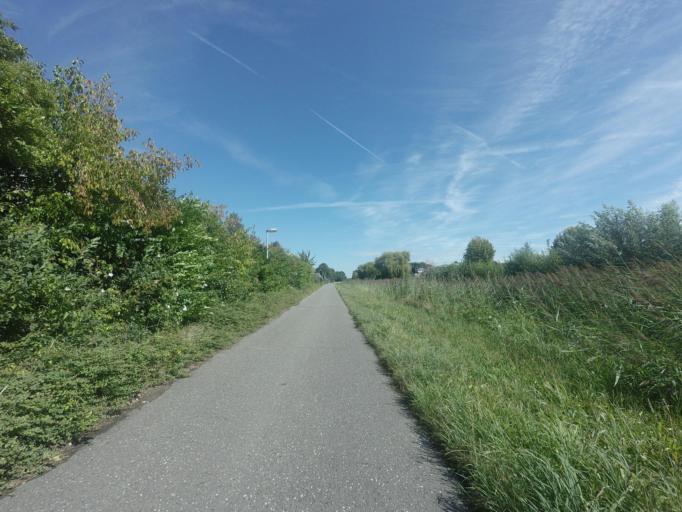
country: NL
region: Overijssel
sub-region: Gemeente Raalte
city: Raalte
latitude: 52.3962
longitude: 6.2920
